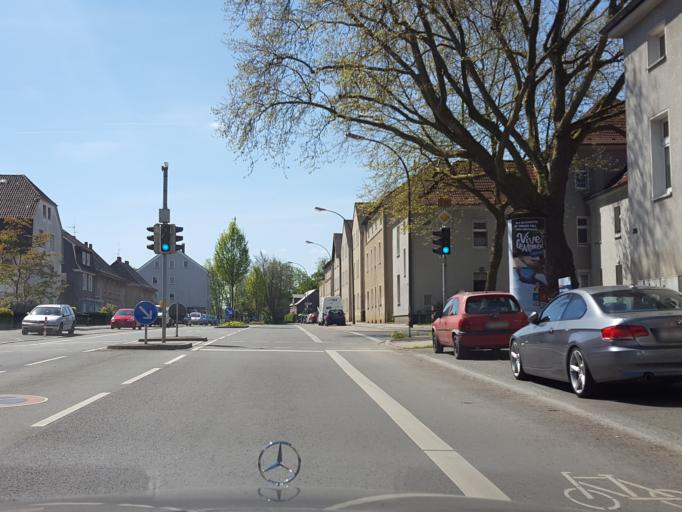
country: DE
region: North Rhine-Westphalia
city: Castrop-Rauxel
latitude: 51.5161
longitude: 7.3229
